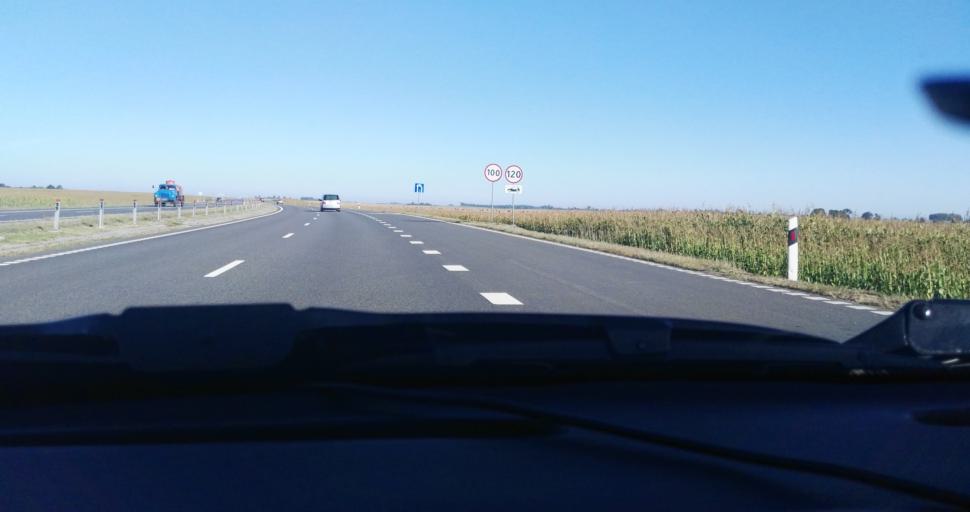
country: BY
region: Gomel
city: Buda-Kashalyova
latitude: 52.5215
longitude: 30.6250
